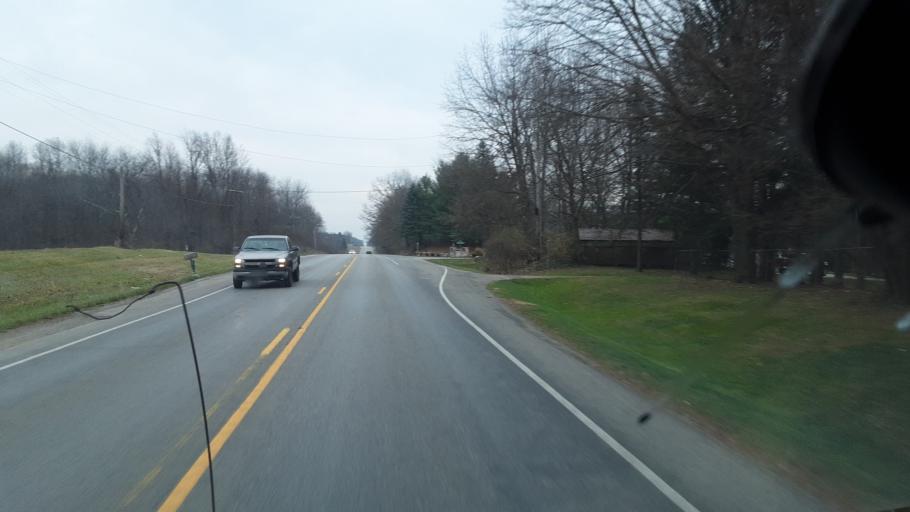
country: US
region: Indiana
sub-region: Elkhart County
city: Middlebury
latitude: 41.7259
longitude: -85.6660
